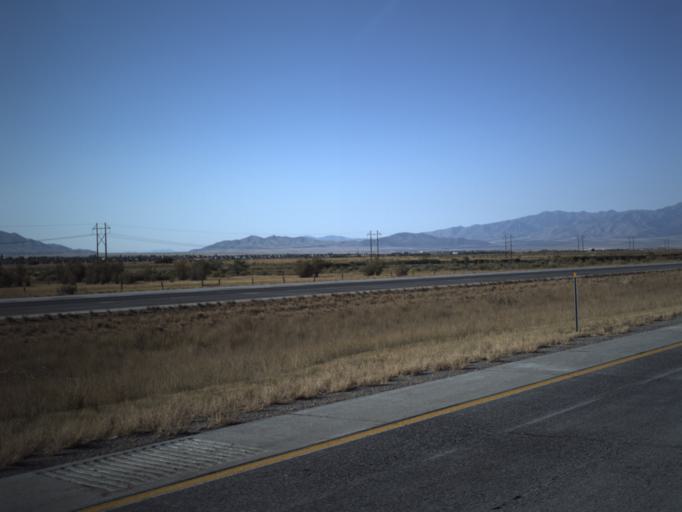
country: US
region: Utah
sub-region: Tooele County
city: Stansbury park
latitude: 40.6699
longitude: -112.2990
